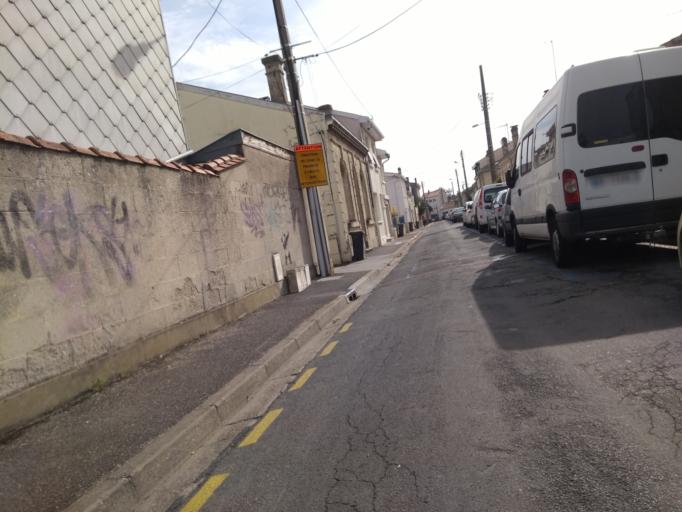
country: FR
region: Aquitaine
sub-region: Departement de la Gironde
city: Talence
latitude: 44.8221
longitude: -0.5902
